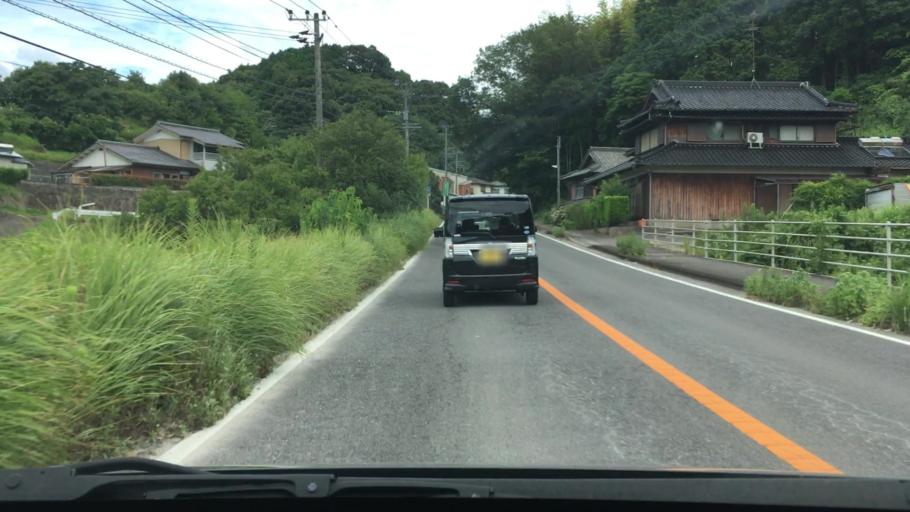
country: JP
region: Nagasaki
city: Togitsu
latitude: 32.9834
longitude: 129.7799
